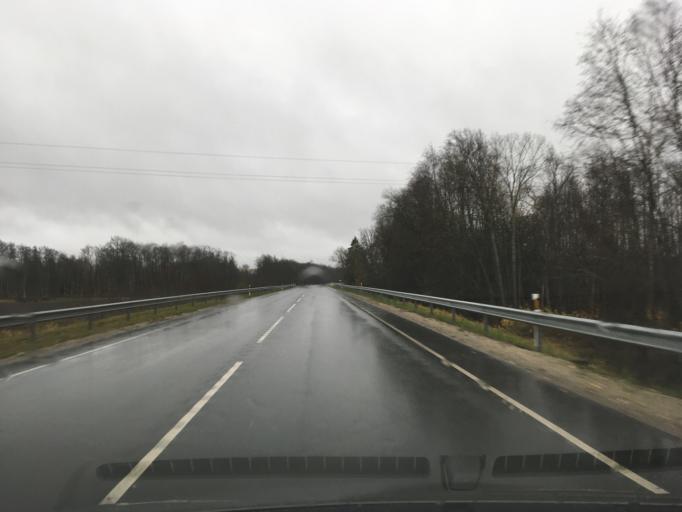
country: EE
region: Laeaene
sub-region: Lihula vald
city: Lihula
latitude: 58.8258
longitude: 24.0562
